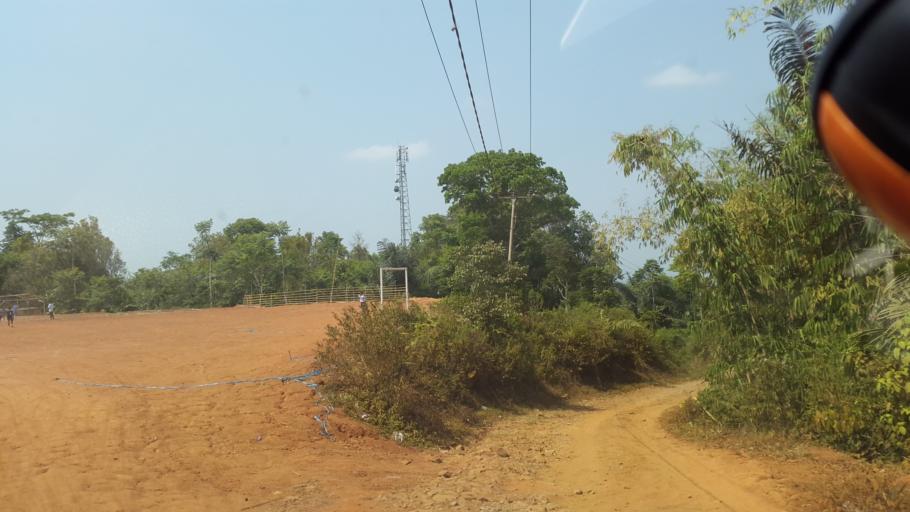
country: ID
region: West Java
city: Sukajaya
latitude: -7.2286
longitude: 106.7608
